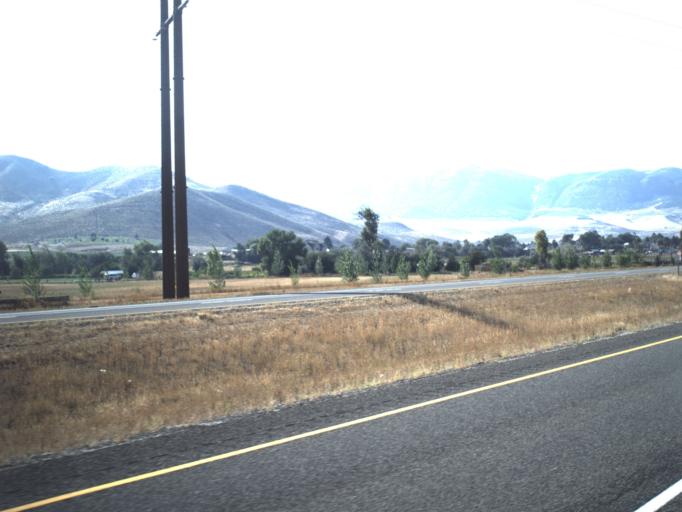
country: US
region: Utah
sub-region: Summit County
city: Coalville
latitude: 41.0104
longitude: -111.4821
